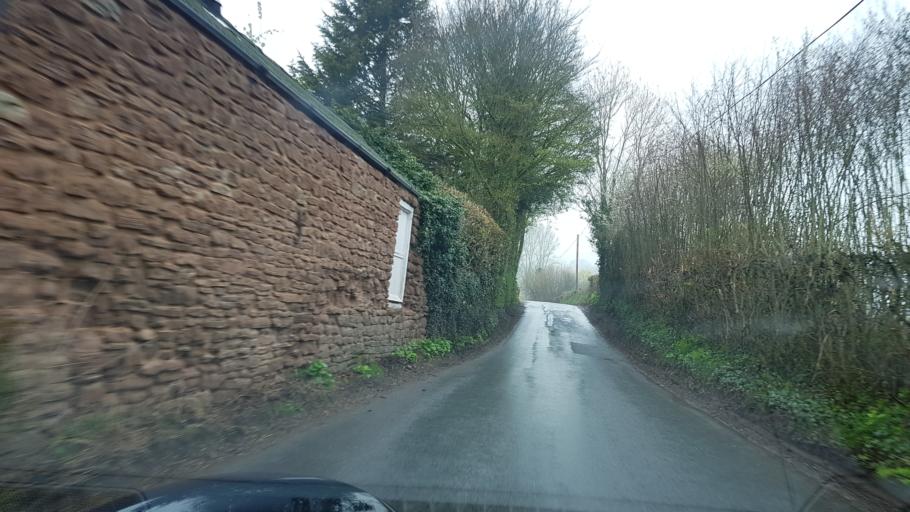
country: GB
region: England
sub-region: Herefordshire
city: Sellack
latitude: 51.9586
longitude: -2.6634
